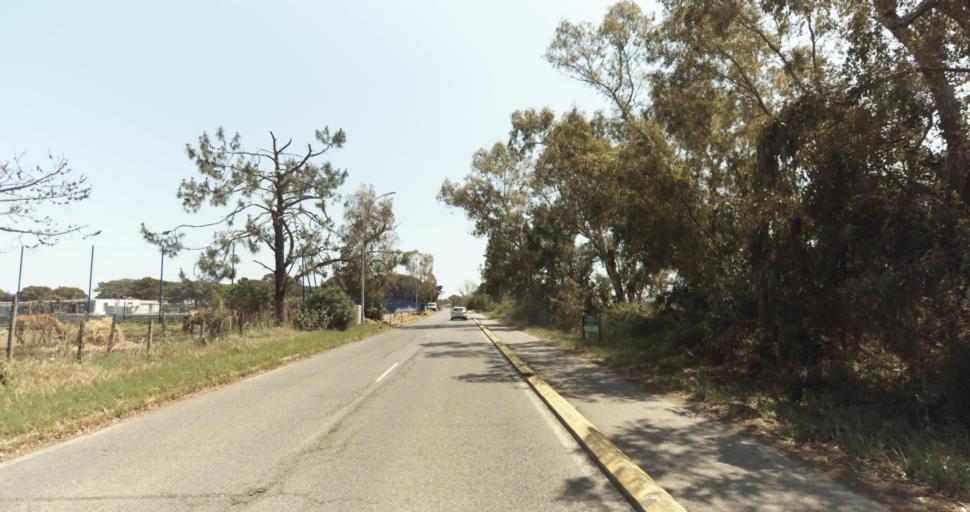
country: FR
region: Corsica
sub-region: Departement de la Haute-Corse
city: Biguglia
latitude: 42.6459
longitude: 9.4546
